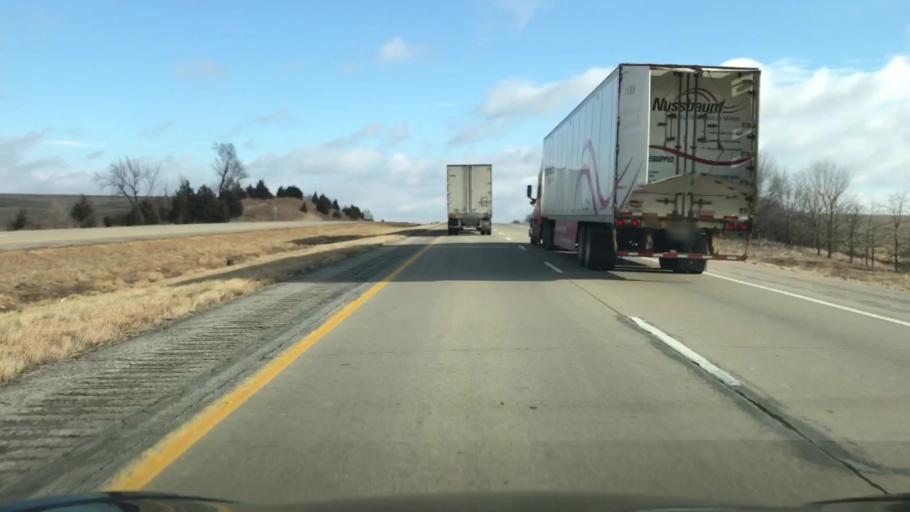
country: US
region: Iowa
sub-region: Cass County
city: Atlantic
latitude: 41.4970
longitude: -94.9197
